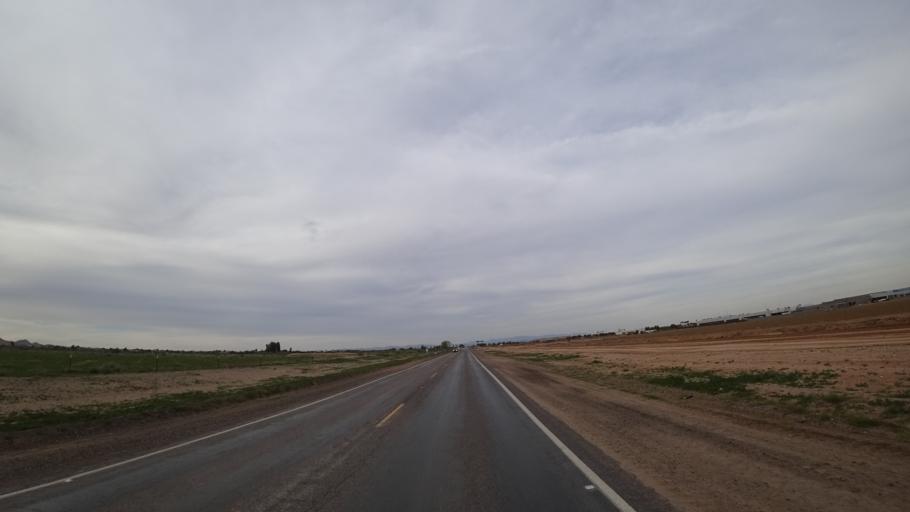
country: US
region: Arizona
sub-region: Maricopa County
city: Citrus Park
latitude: 33.6005
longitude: -112.4268
